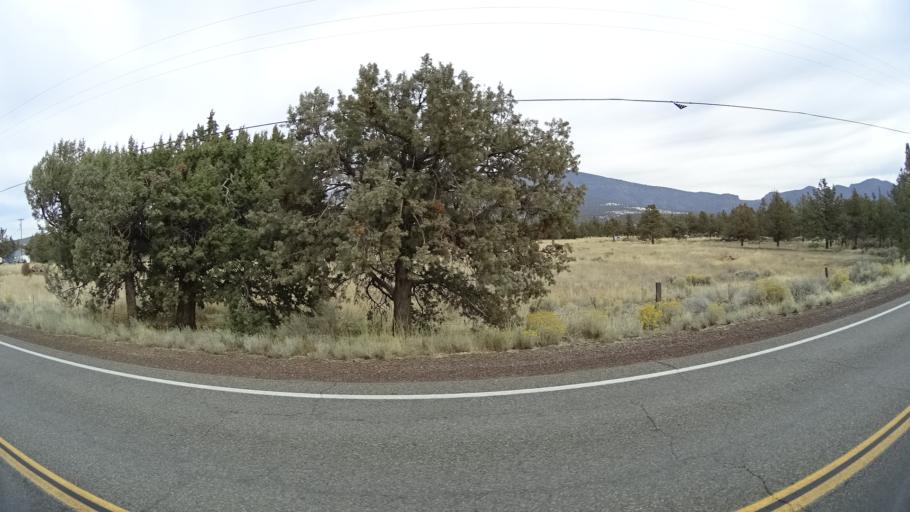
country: US
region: California
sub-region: Siskiyou County
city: Weed
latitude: 41.5907
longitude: -122.3047
